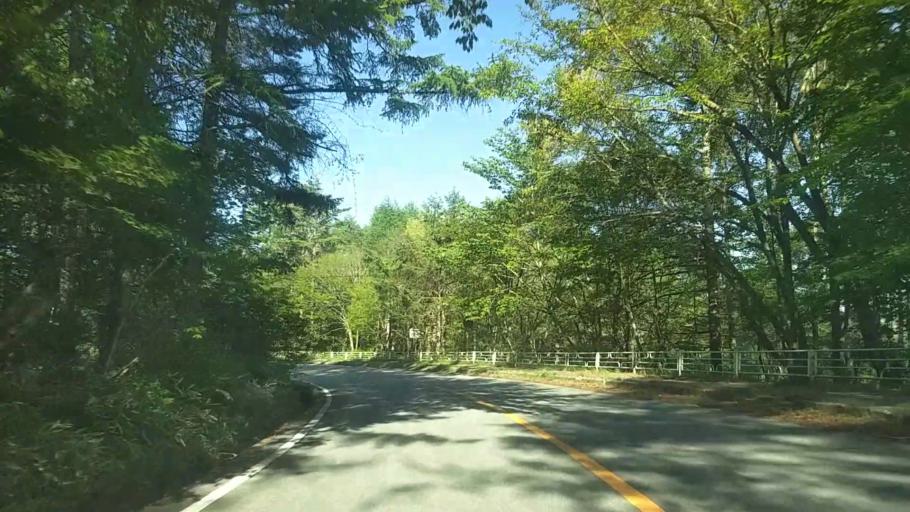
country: JP
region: Yamanashi
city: Nirasaki
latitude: 35.9021
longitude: 138.3837
